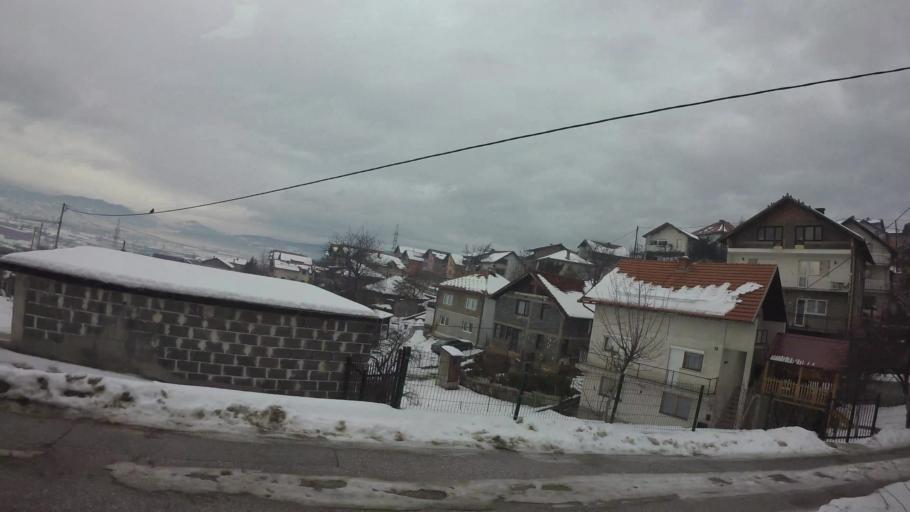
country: BA
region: Federation of Bosnia and Herzegovina
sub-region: Kanton Sarajevo
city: Sarajevo
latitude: 43.8557
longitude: 18.3302
